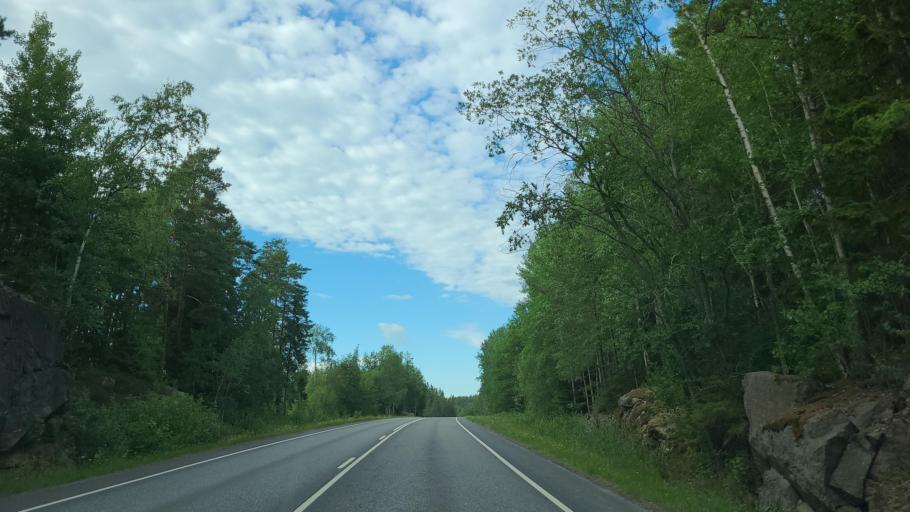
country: FI
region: Varsinais-Suomi
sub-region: Turku
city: Merimasku
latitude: 60.4363
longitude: 21.8958
